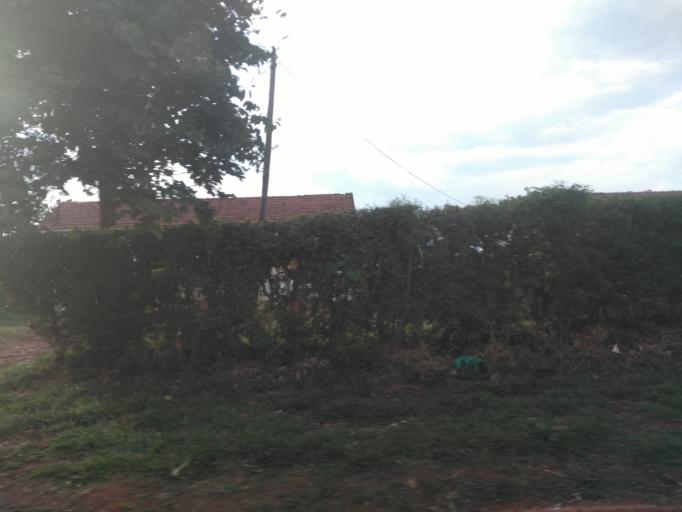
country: UG
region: Eastern Region
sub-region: Jinja District
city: Jinja
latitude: 0.4231
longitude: 33.2109
